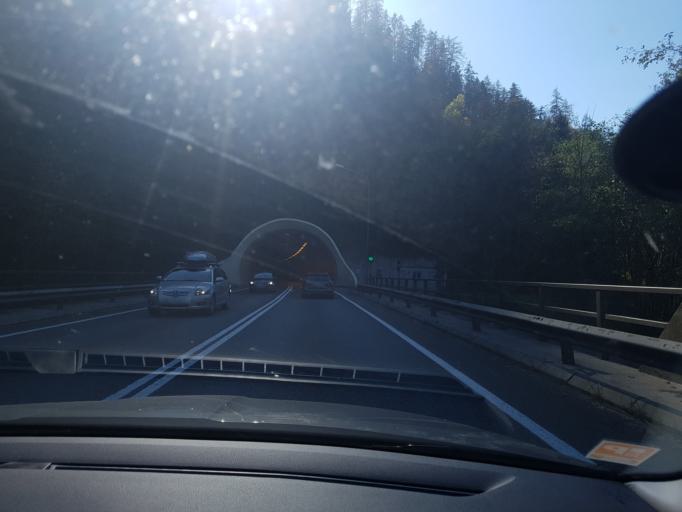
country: AT
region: Salzburg
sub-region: Politischer Bezirk Zell am See
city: Unken
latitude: 47.6553
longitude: 12.7415
